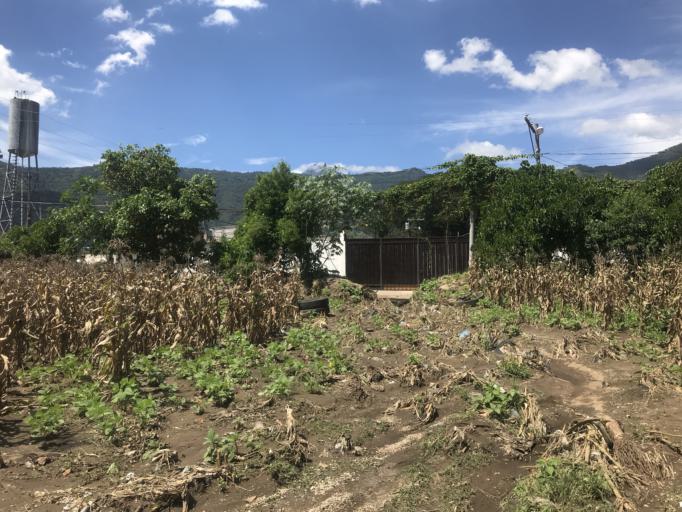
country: GT
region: Guatemala
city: Amatitlan
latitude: 14.4801
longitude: -90.6327
